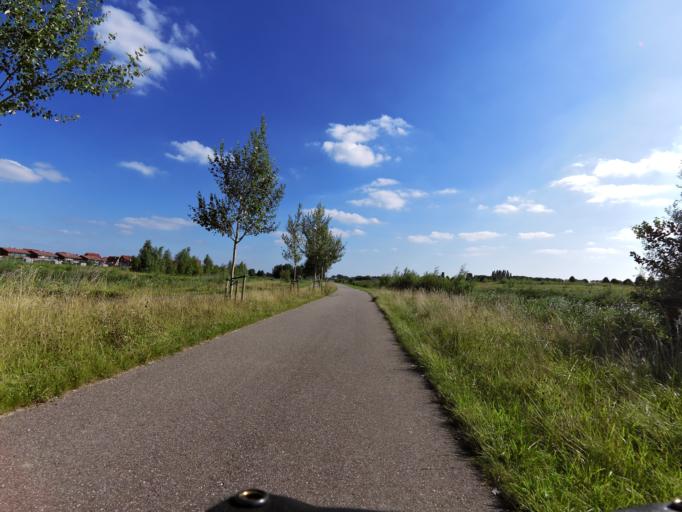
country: NL
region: South Holland
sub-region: Gemeente Binnenmaas
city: Heinenoord
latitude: 51.8595
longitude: 4.4610
